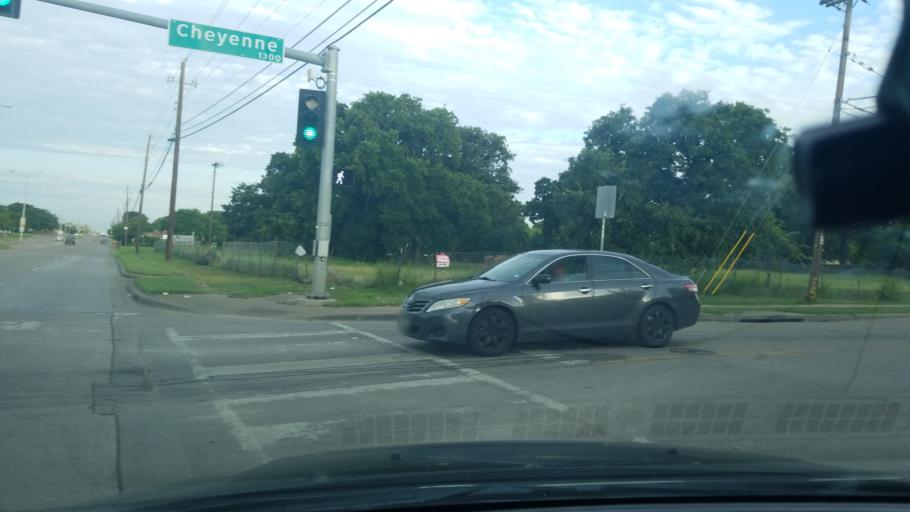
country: US
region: Texas
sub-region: Dallas County
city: Balch Springs
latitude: 32.7342
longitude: -96.6397
